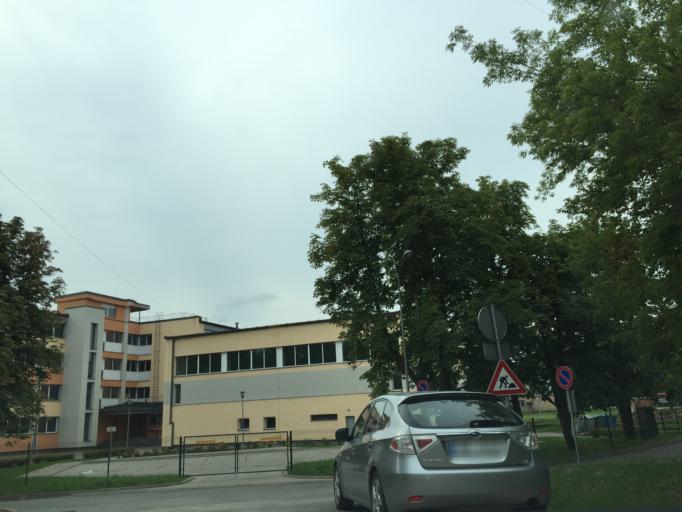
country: LV
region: Ogre
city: Ogre
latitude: 56.8250
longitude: 24.5953
